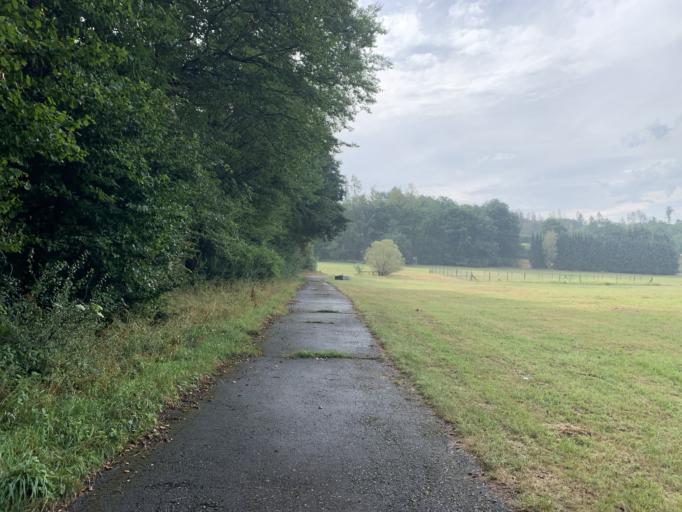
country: DE
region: Rheinland-Pfalz
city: Holzhausen an der Haide
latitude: 50.2176
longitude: 7.9220
